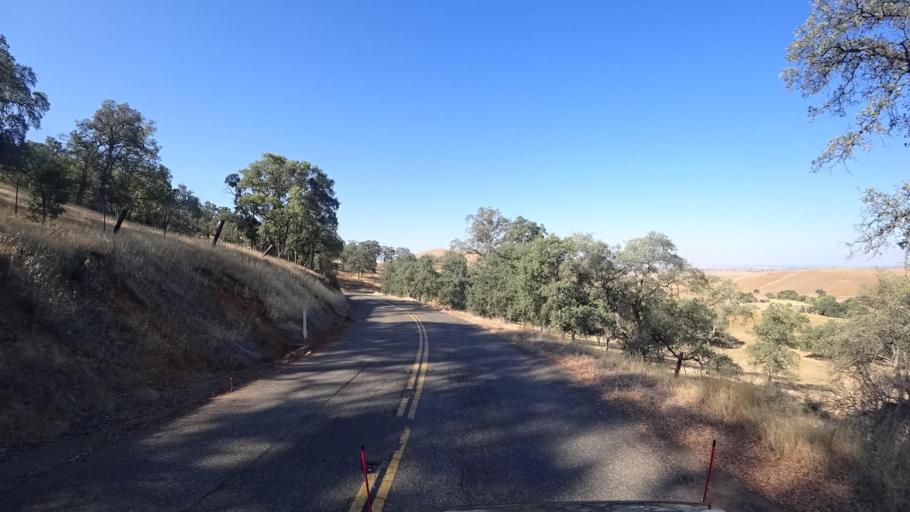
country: US
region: California
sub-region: Mariposa County
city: Mariposa
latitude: 37.5523
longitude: -120.1763
